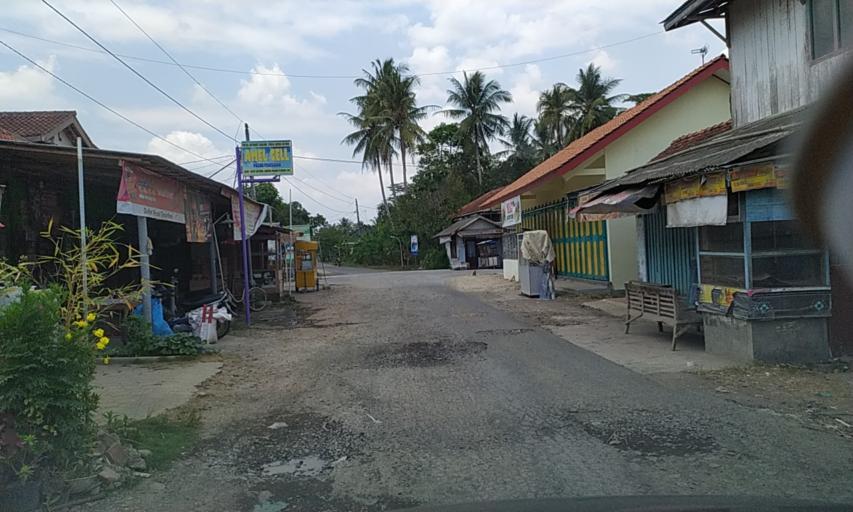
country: ID
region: Central Java
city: Sidaurip
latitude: -7.5487
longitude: 108.7558
